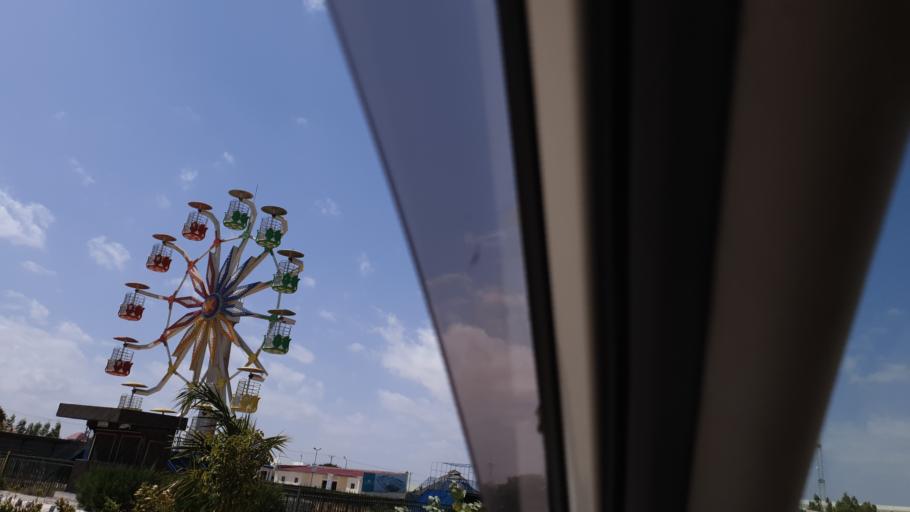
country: SO
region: Banaadir
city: Mogadishu
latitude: 2.1427
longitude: 45.3250
